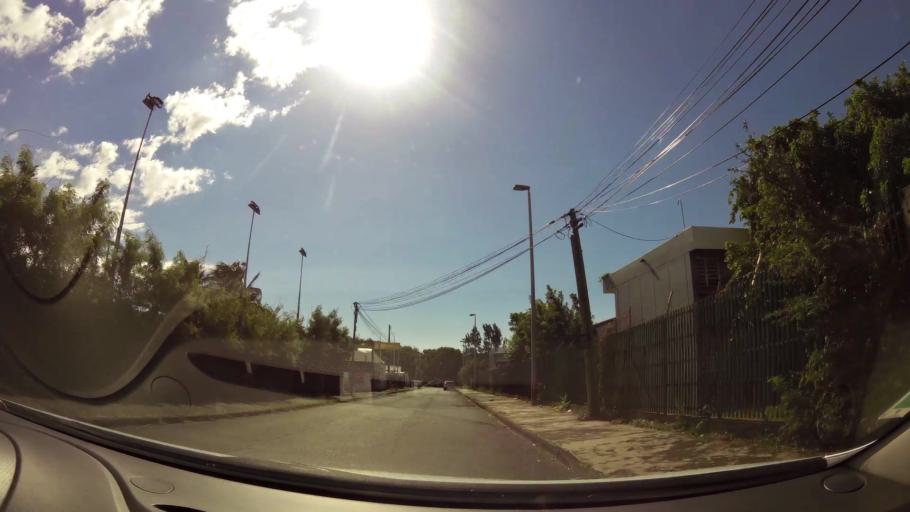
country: RE
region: Reunion
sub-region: Reunion
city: Saint-Denis
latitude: -20.8877
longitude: 55.4958
